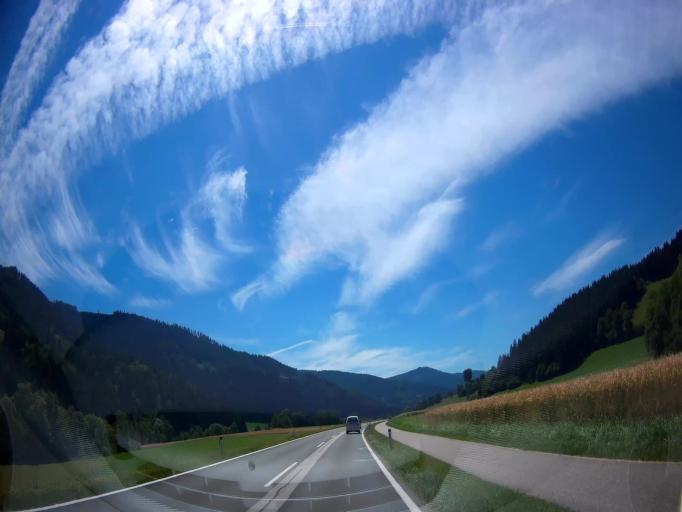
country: AT
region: Carinthia
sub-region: Politischer Bezirk Sankt Veit an der Glan
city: Strassburg
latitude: 46.8902
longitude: 14.3187
